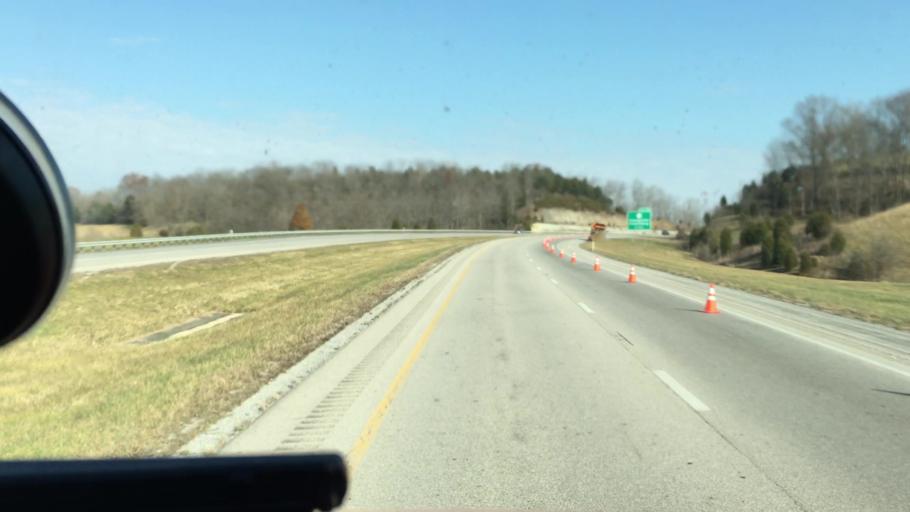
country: US
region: Kentucky
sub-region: Bath County
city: Owingsville
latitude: 38.1224
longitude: -83.7931
